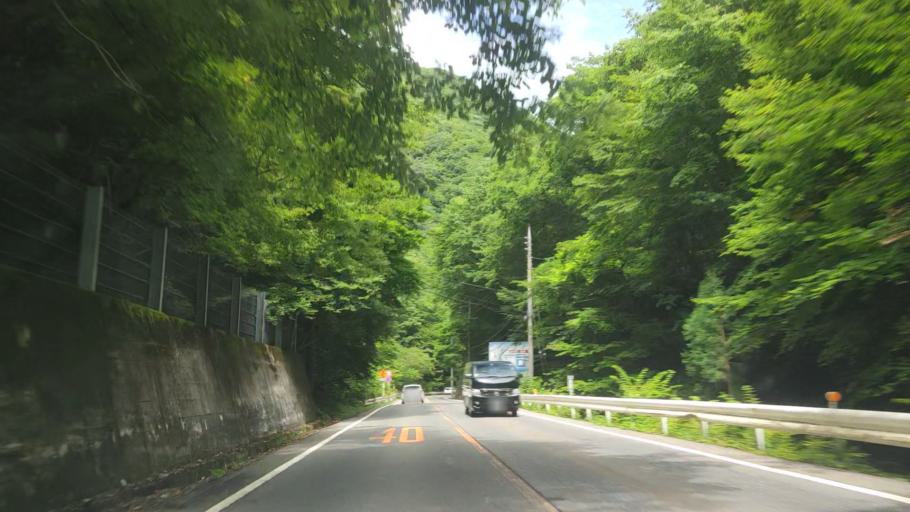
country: JP
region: Gunma
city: Numata
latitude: 36.7974
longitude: 139.2842
